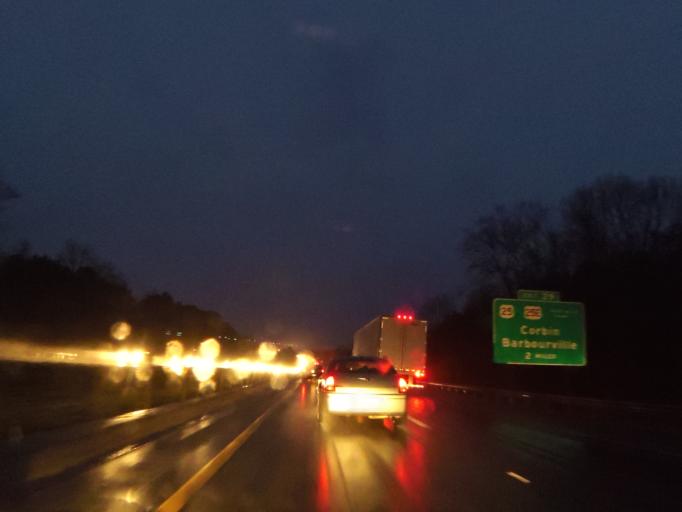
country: US
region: Kentucky
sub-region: Laurel County
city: North Corbin
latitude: 37.0078
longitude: -84.1038
